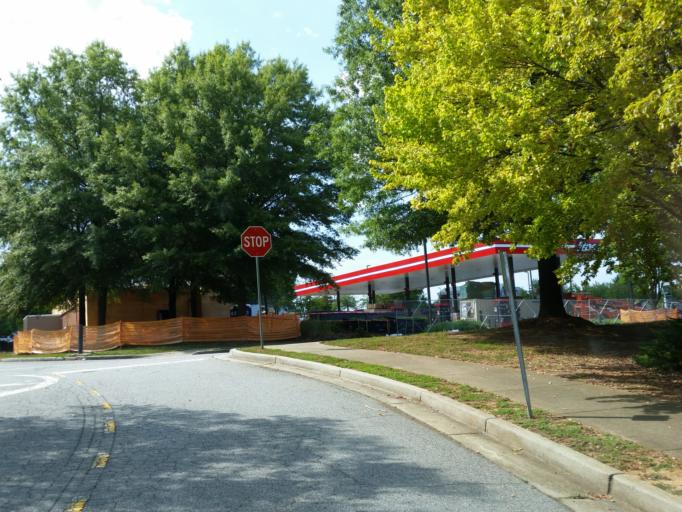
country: US
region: Georgia
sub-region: Fulton County
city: Roswell
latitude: 34.0394
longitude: -84.3222
